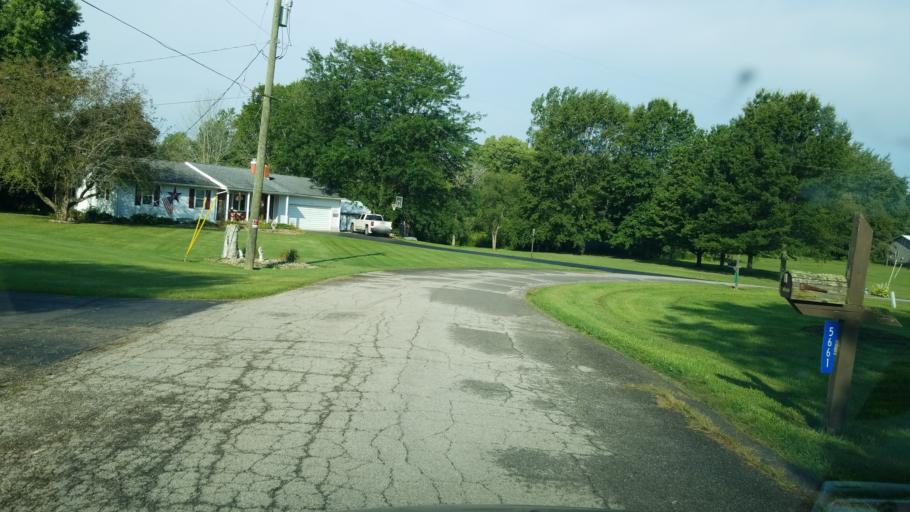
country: US
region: Ohio
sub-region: Crawford County
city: Galion
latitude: 40.7435
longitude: -82.8459
